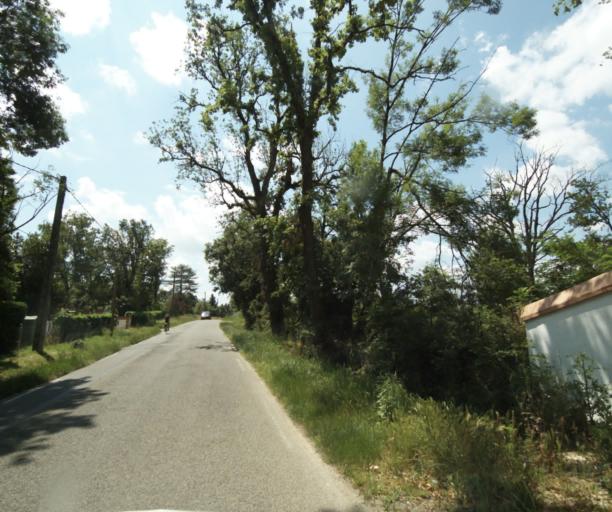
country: FR
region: Midi-Pyrenees
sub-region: Departement du Tarn-et-Garonne
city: Montauban
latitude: 44.0423
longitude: 1.3477
